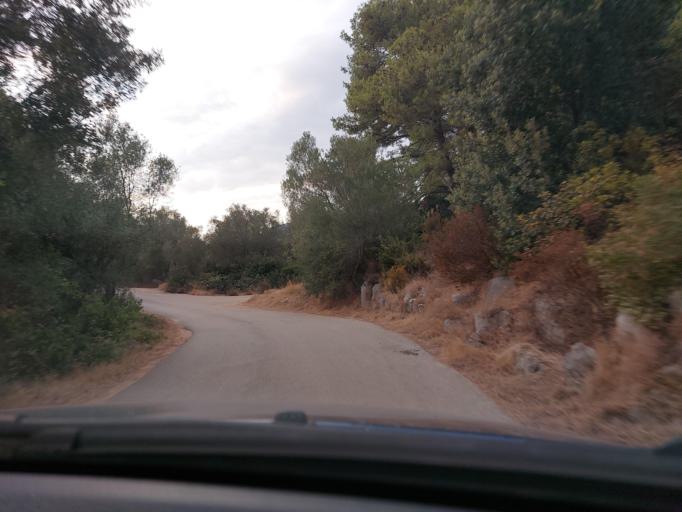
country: HR
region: Dubrovacko-Neretvanska
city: Smokvica
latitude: 42.7609
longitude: 16.9154
